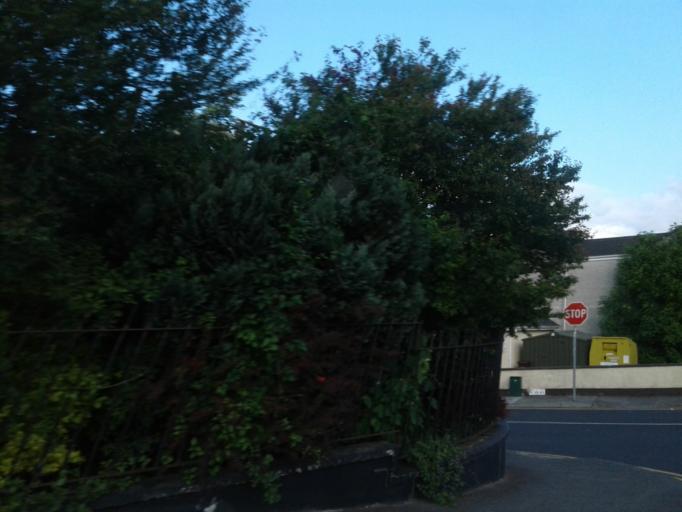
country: IE
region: Connaught
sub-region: County Galway
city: Ballinasloe
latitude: 53.3277
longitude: -8.2229
